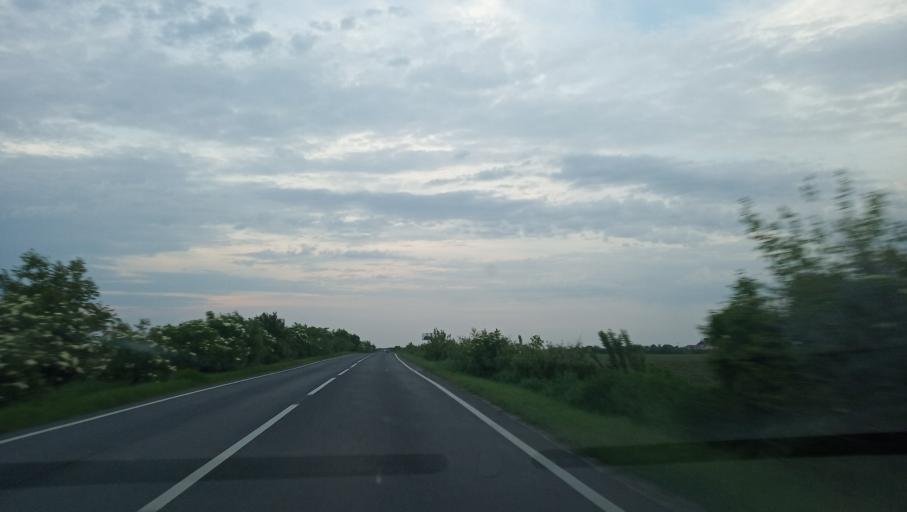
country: RO
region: Timis
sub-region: Comuna Voiteg
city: Voiteg
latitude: 45.4869
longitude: 21.2342
